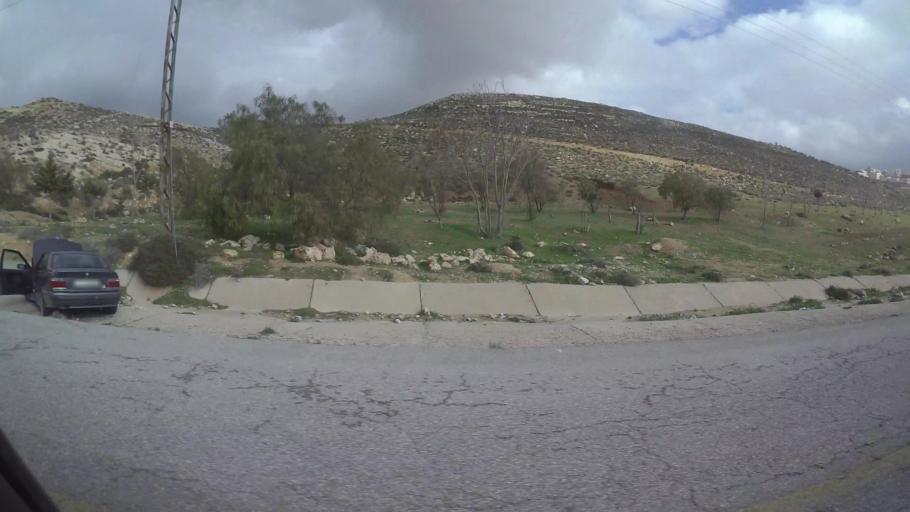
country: JO
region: Amman
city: Al Jubayhah
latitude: 32.0802
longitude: 35.8793
